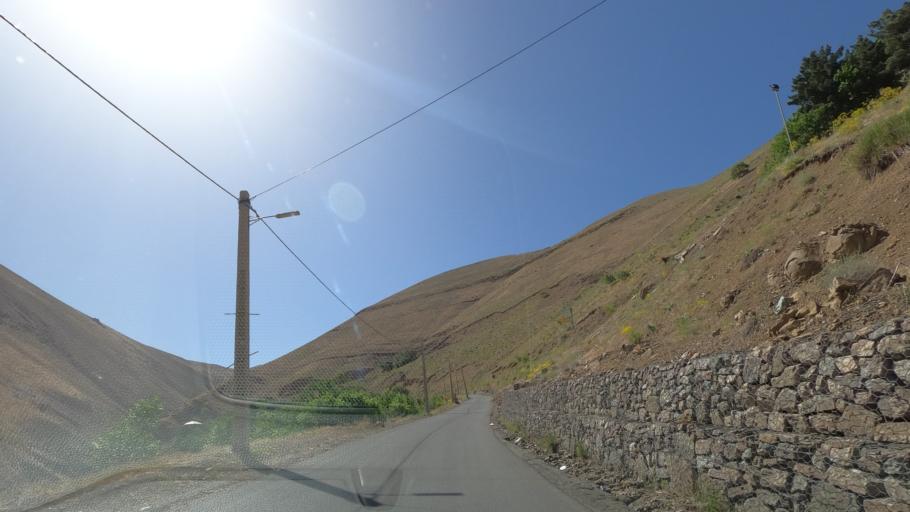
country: IR
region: Alborz
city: Karaj
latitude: 35.9419
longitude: 51.0835
